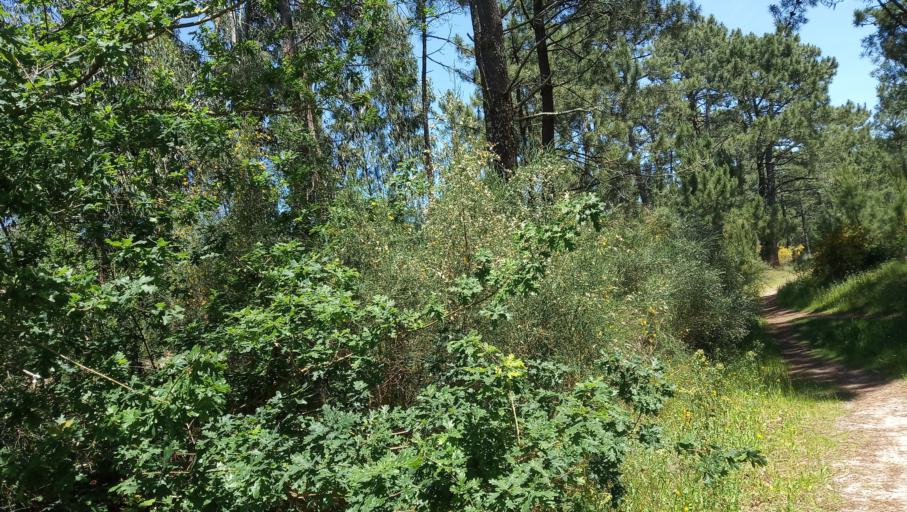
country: ES
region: Galicia
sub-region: Provincia de Pontevedra
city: A Guarda
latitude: 41.8745
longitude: -8.8663
